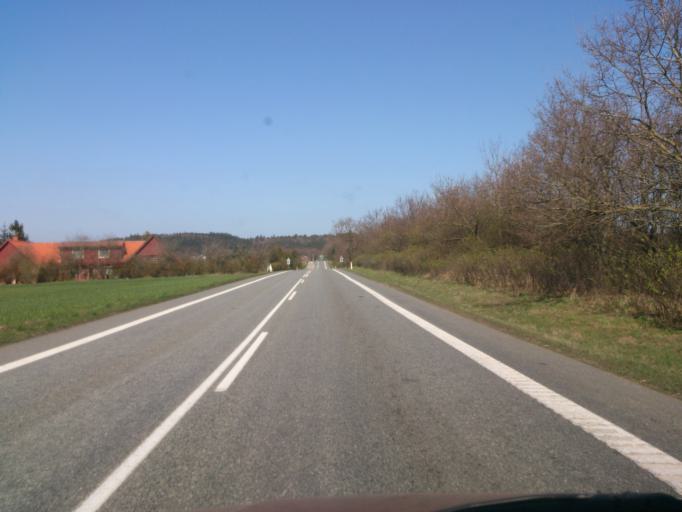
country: DK
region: Central Jutland
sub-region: Favrskov Kommune
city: Ulstrup
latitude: 56.4470
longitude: 9.7399
